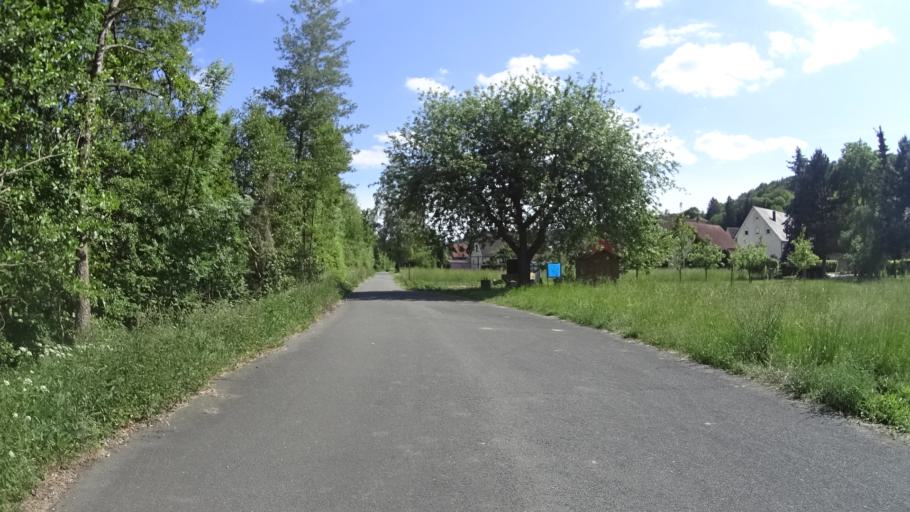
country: DE
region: Baden-Wuerttemberg
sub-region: Karlsruhe Region
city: Hardheim
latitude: 49.5826
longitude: 9.4854
